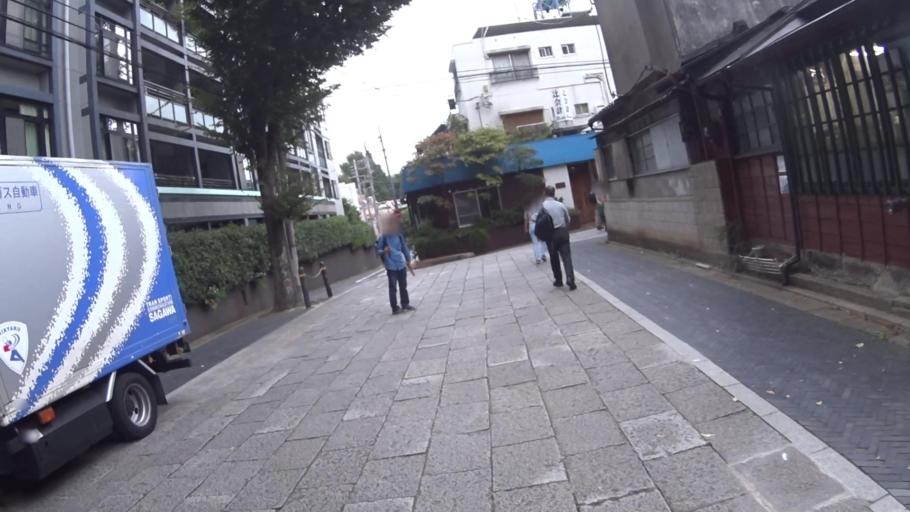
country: JP
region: Tokyo
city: Tokyo
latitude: 35.7220
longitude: 139.7140
